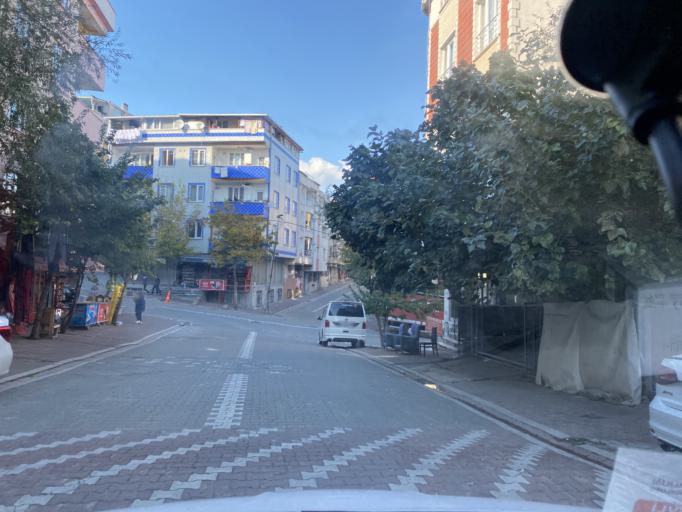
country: TR
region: Istanbul
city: Esenyurt
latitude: 41.0367
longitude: 28.6511
